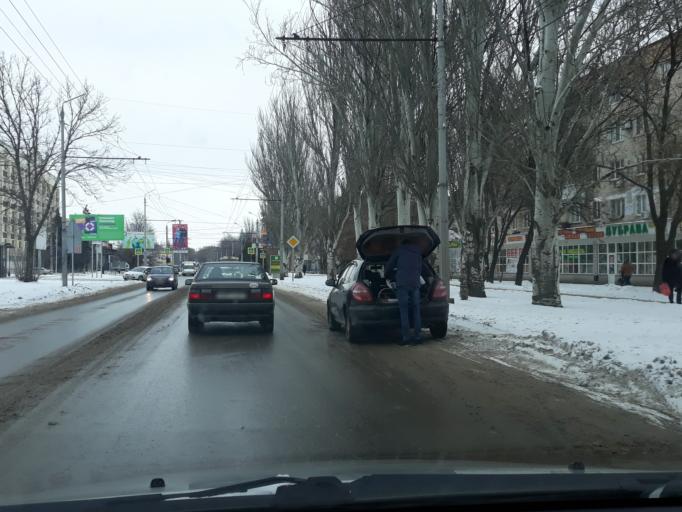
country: RU
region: Rostov
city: Taganrog
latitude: 47.2484
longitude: 38.9178
